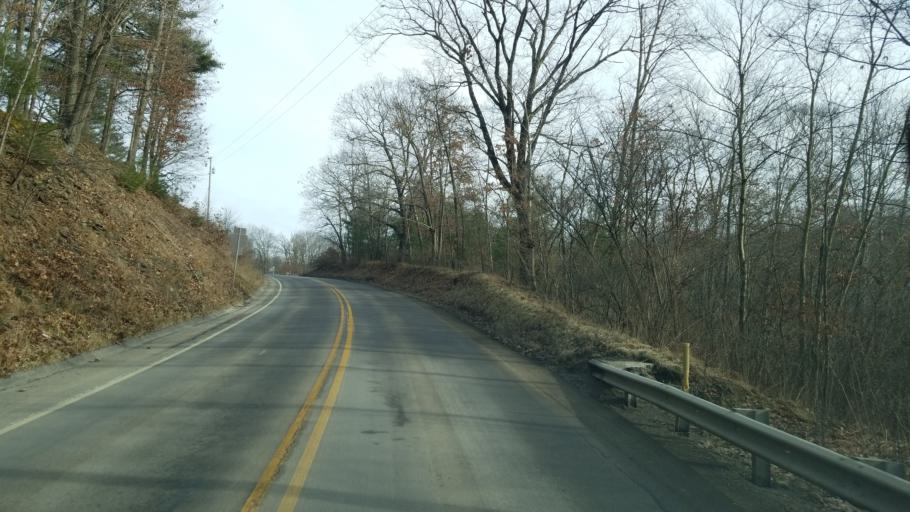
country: US
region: Pennsylvania
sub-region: Jefferson County
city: Punxsutawney
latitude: 40.9029
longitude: -79.0384
